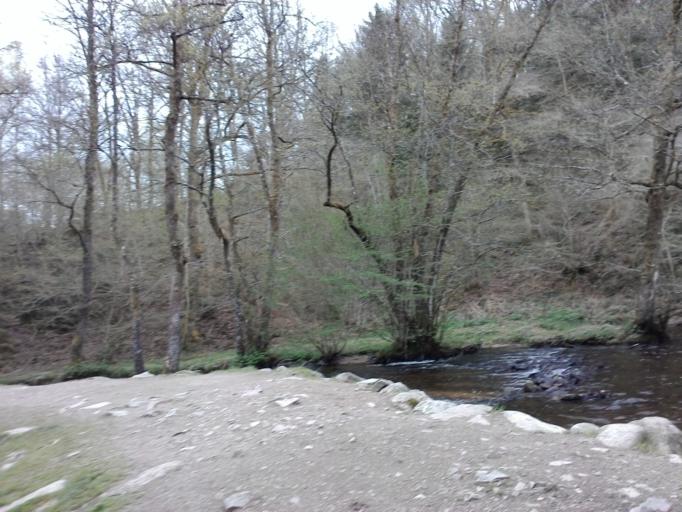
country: FR
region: Bourgogne
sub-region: Departement de la Cote-d'Or
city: Saulieu
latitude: 47.2438
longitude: 4.0623
